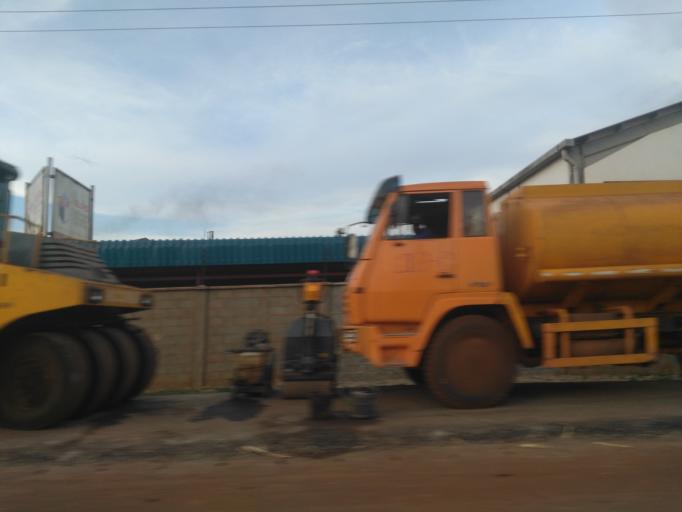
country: UG
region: Eastern Region
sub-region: Jinja District
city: Jinja
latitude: 0.4392
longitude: 33.1816
